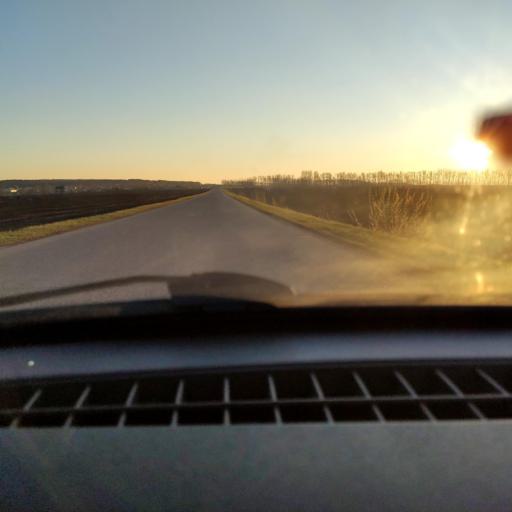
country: RU
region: Bashkortostan
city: Avdon
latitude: 54.5433
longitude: 55.6486
